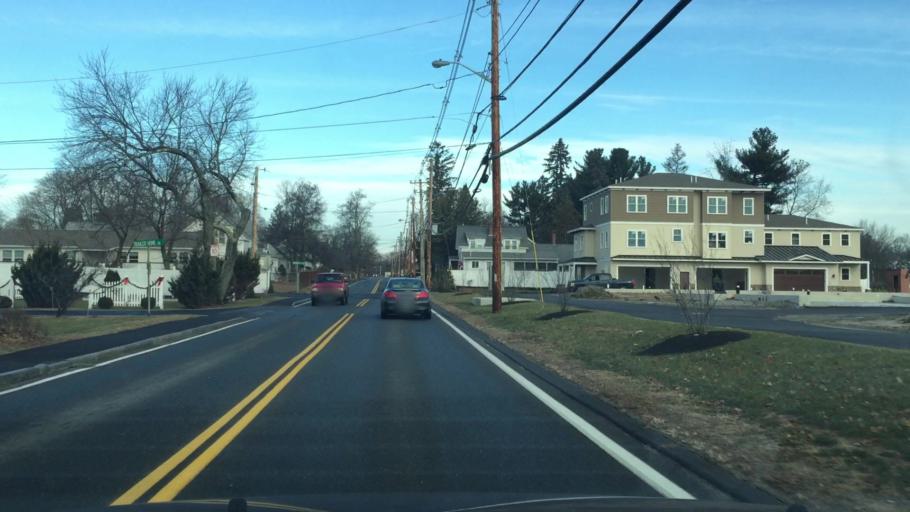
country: US
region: New Hampshire
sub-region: Rockingham County
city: Salem
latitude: 42.7779
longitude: -71.2311
